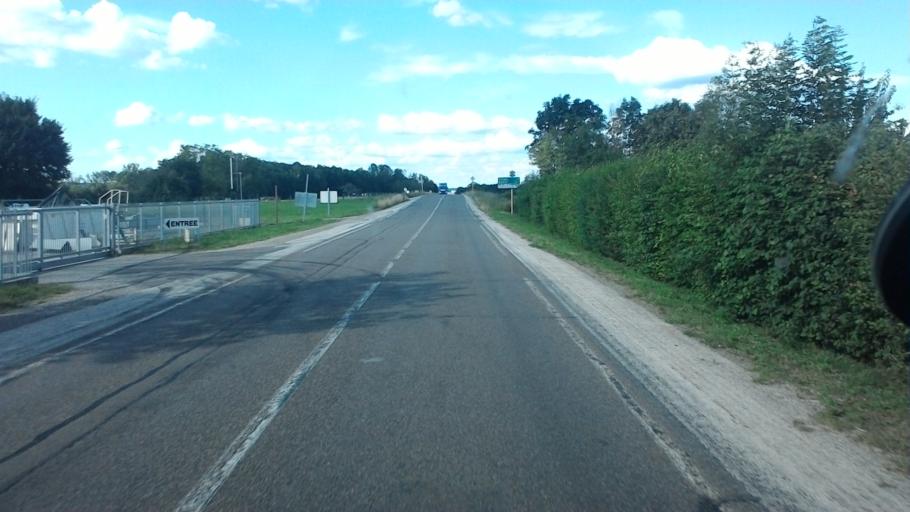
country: FR
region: Franche-Comte
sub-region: Departement de la Haute-Saone
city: Frotey-les-Vesoul
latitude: 47.6988
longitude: 6.2867
